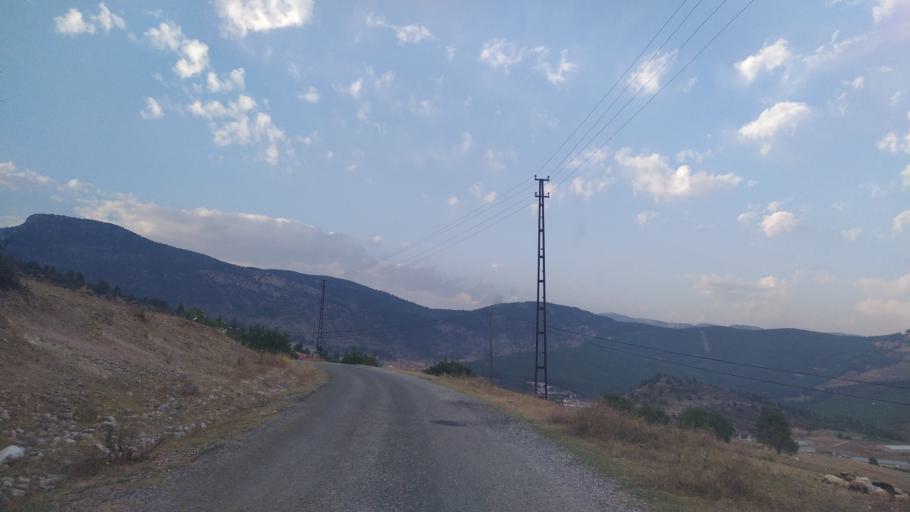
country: TR
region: Mersin
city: Camliyayla
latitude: 37.2267
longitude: 34.7104
